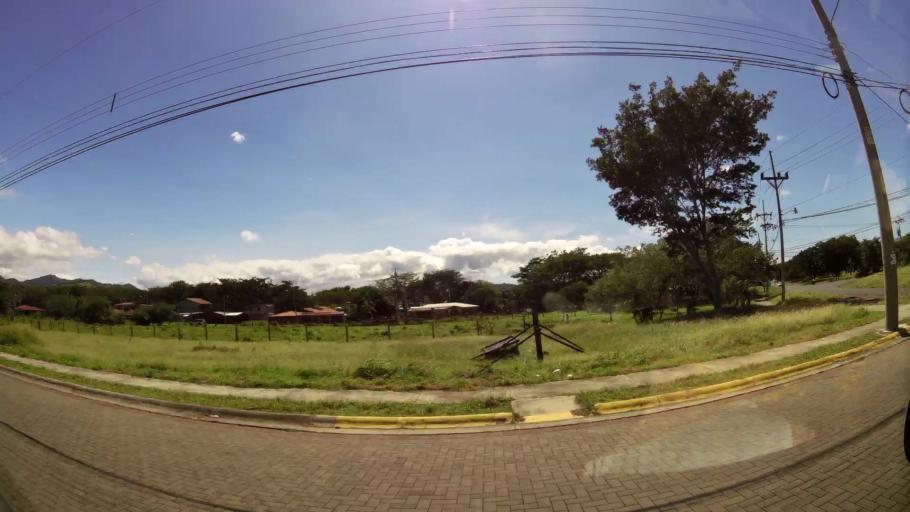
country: CR
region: Guanacaste
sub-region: Canton de Canas
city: Canas
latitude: 10.4327
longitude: -85.0856
